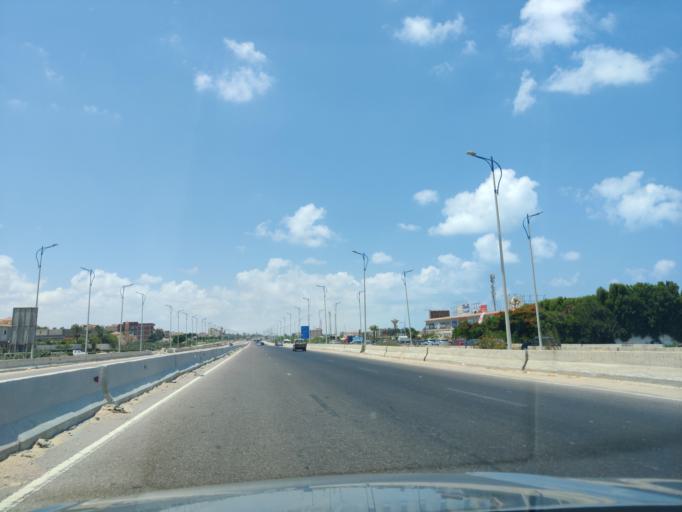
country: EG
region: Alexandria
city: Alexandria
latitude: 30.9787
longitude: 29.5753
